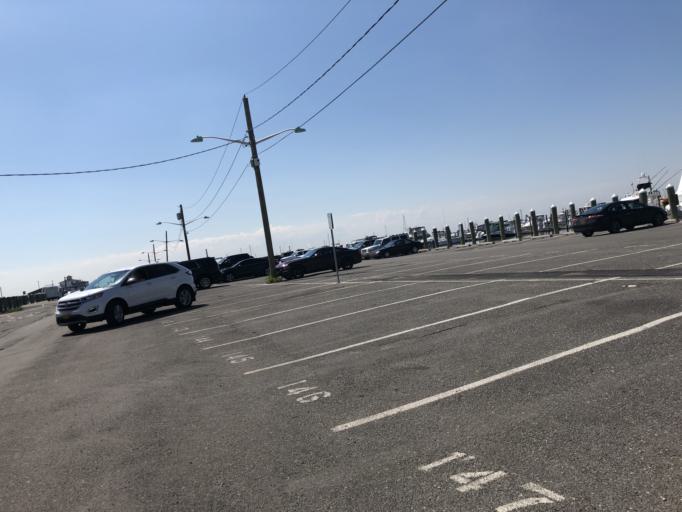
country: US
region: New York
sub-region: Suffolk County
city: Bay Shore
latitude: 40.7150
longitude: -73.2406
